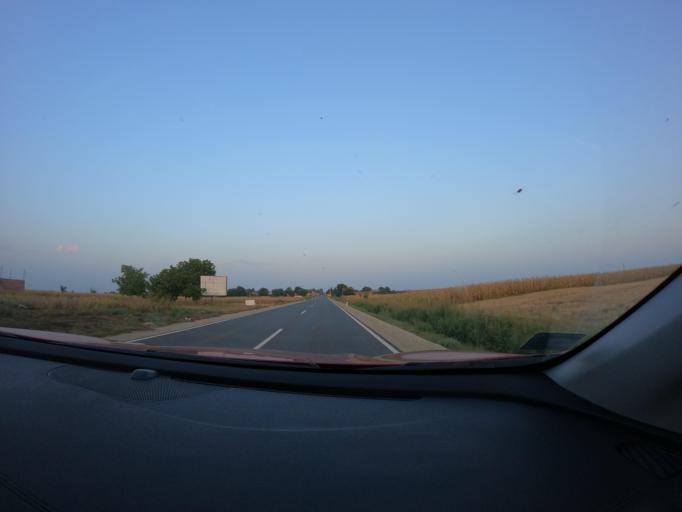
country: RS
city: Putinci
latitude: 45.0041
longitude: 19.9256
